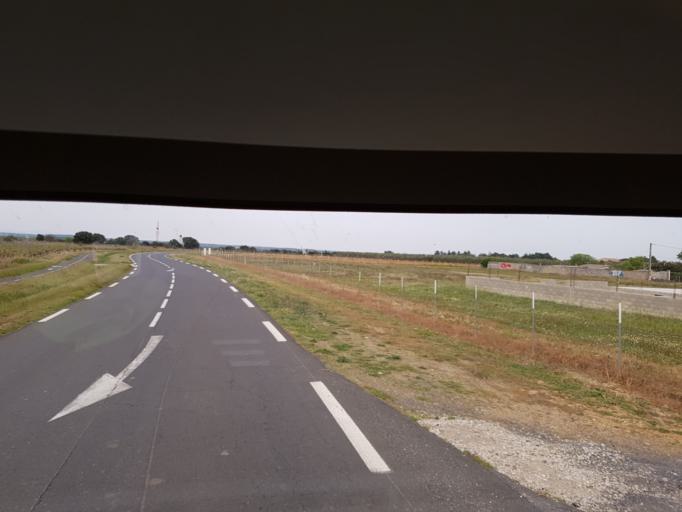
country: FR
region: Languedoc-Roussillon
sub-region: Departement de l'Herault
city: Serignan
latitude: 43.2728
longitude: 3.2623
